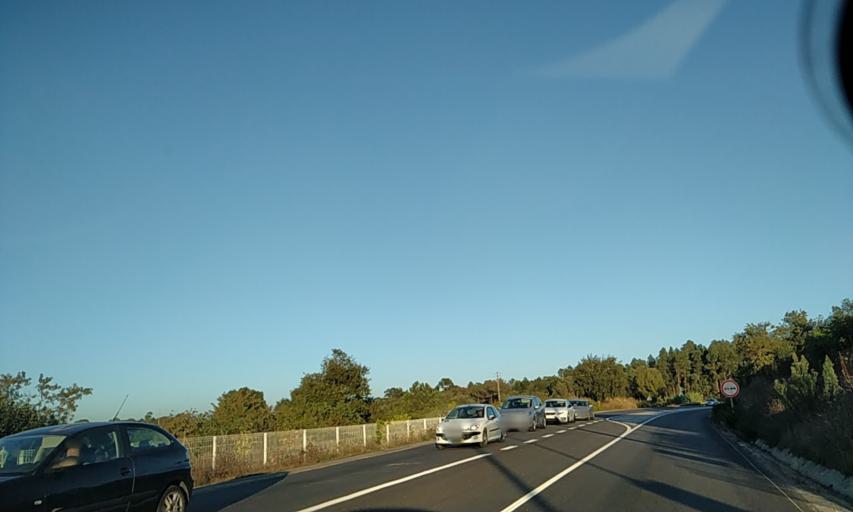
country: PT
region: Aveiro
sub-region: Oliveira do Bairro
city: Oia
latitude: 40.5473
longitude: -8.5377
